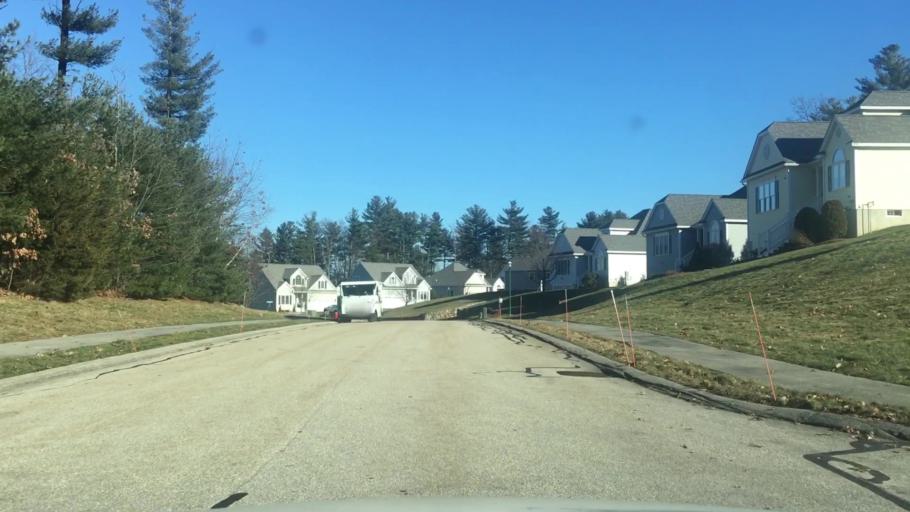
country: US
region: New Hampshire
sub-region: Rockingham County
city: Londonderry
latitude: 42.8886
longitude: -71.4164
